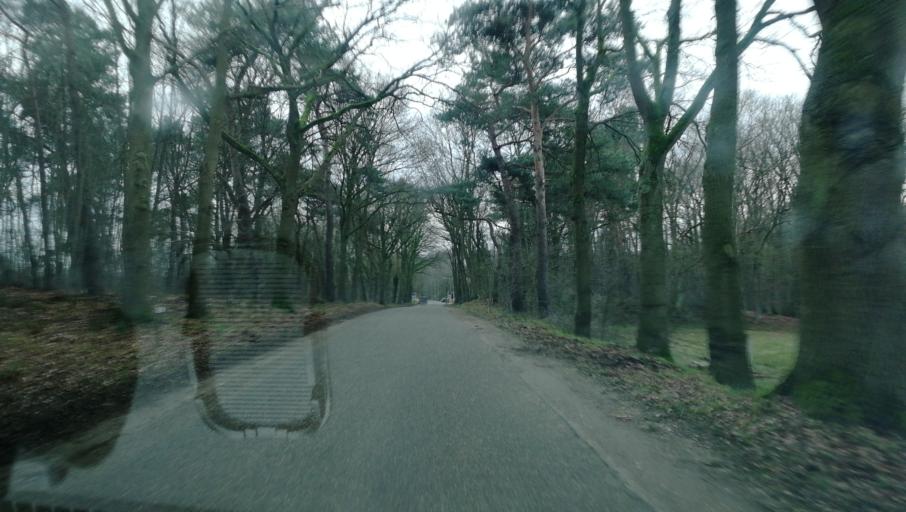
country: NL
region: Limburg
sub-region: Gemeente Venlo
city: Venlo
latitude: 51.4098
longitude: 6.1918
